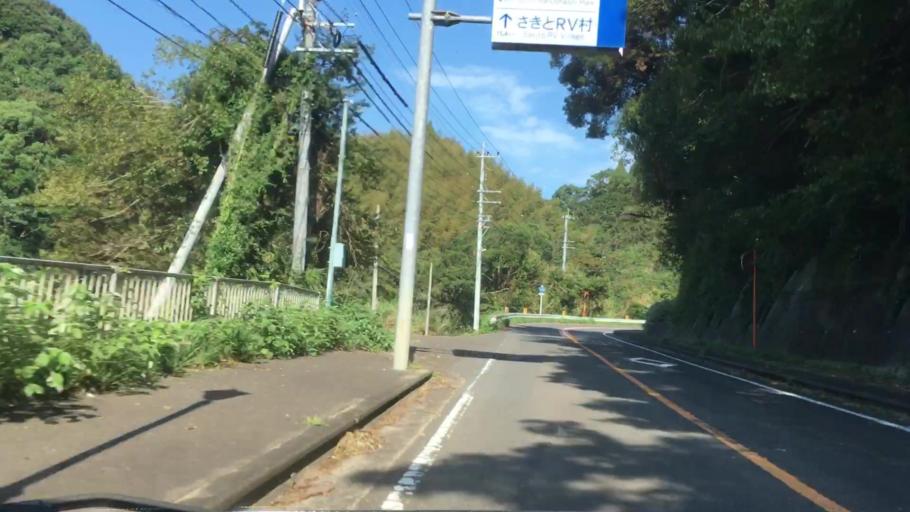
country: JP
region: Nagasaki
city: Sasebo
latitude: 33.0251
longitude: 129.6540
